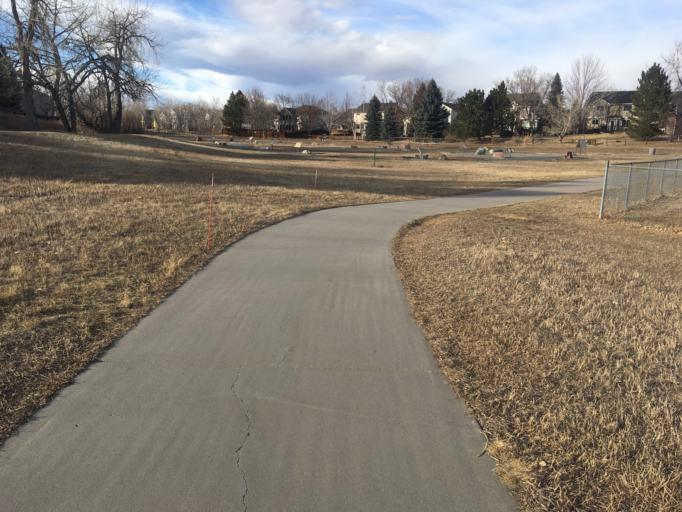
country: US
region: Colorado
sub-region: Broomfield County
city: Broomfield
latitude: 39.9366
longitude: -105.0818
